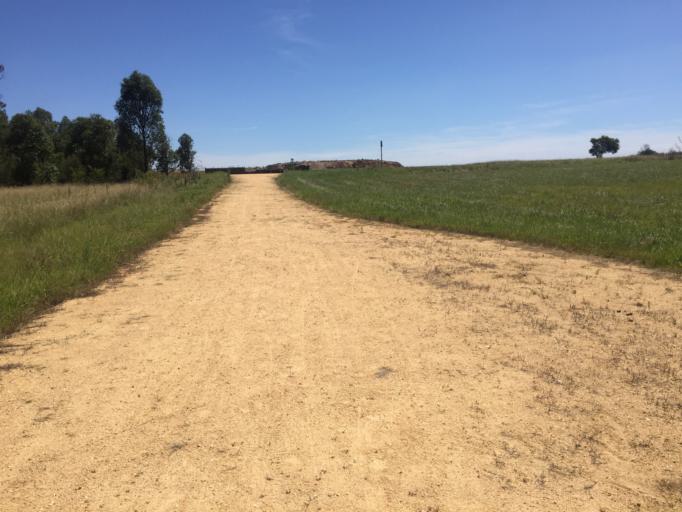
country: AU
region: New South Wales
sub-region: Blacktown
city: Doonside
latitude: -33.7861
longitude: 150.8686
